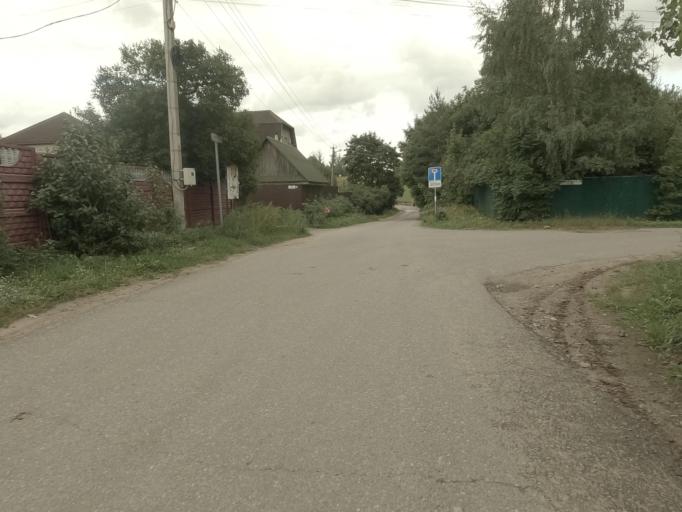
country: RU
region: Leningrad
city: Koltushi
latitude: 59.8894
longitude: 30.6925
